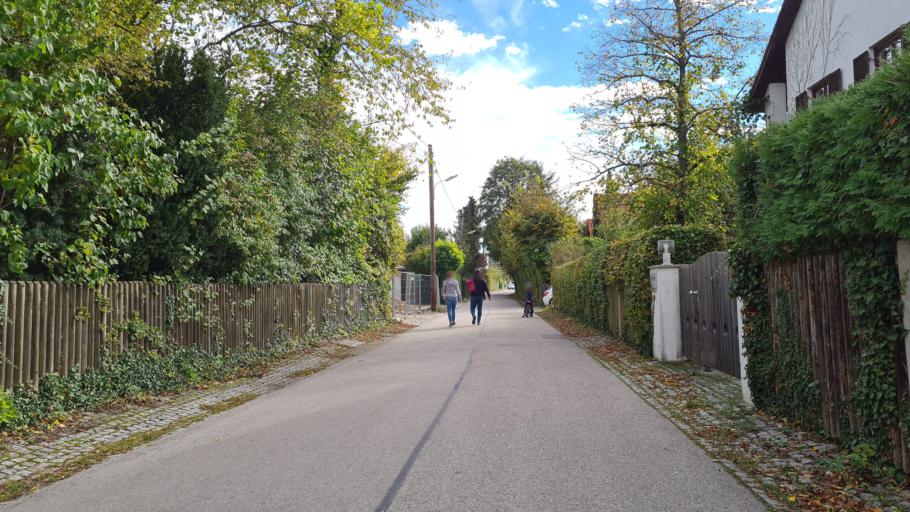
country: DE
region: Bavaria
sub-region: Upper Bavaria
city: Krailling
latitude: 48.0861
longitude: 11.3993
